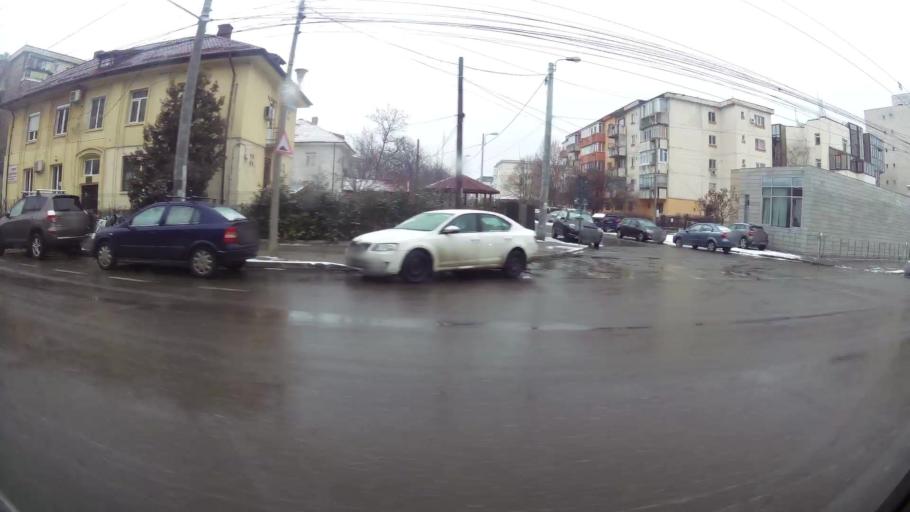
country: RO
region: Prahova
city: Ploiesti
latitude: 44.9388
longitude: 26.0037
